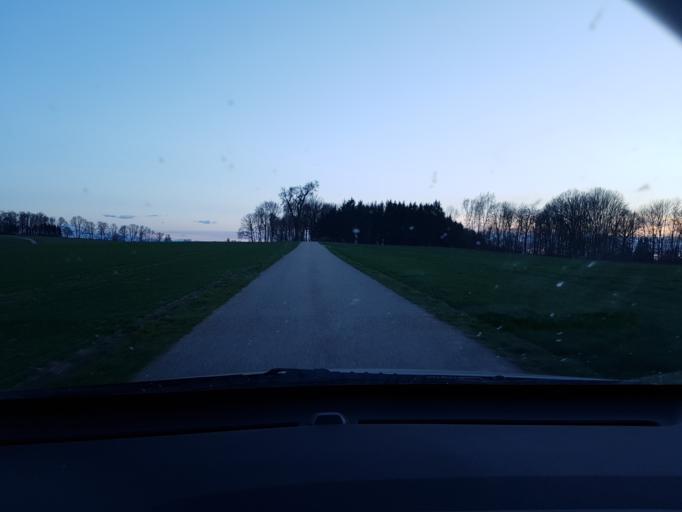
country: AT
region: Upper Austria
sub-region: Politischer Bezirk Linz-Land
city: Ansfelden
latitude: 48.1790
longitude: 14.3228
